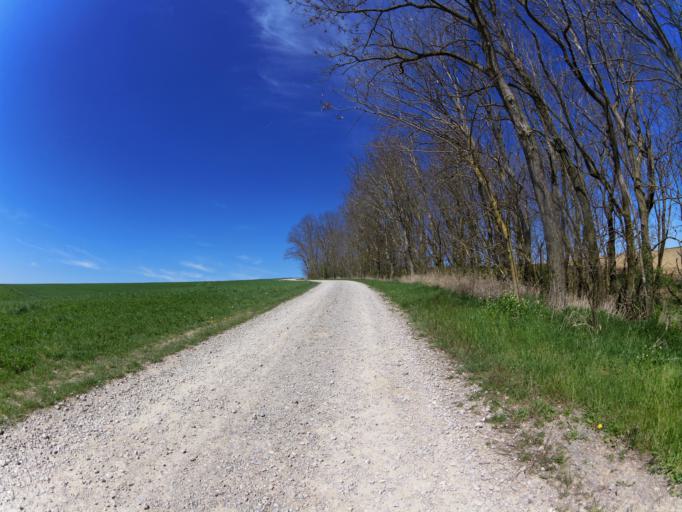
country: DE
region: Bavaria
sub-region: Regierungsbezirk Unterfranken
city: Winterhausen
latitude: 49.6936
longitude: 9.9880
